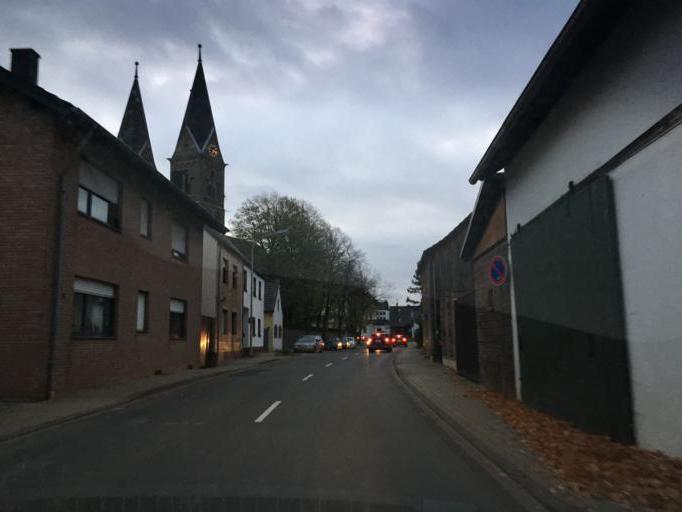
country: DE
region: North Rhine-Westphalia
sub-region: Regierungsbezirk Koln
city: Vettweiss
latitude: 50.7640
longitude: 6.5597
